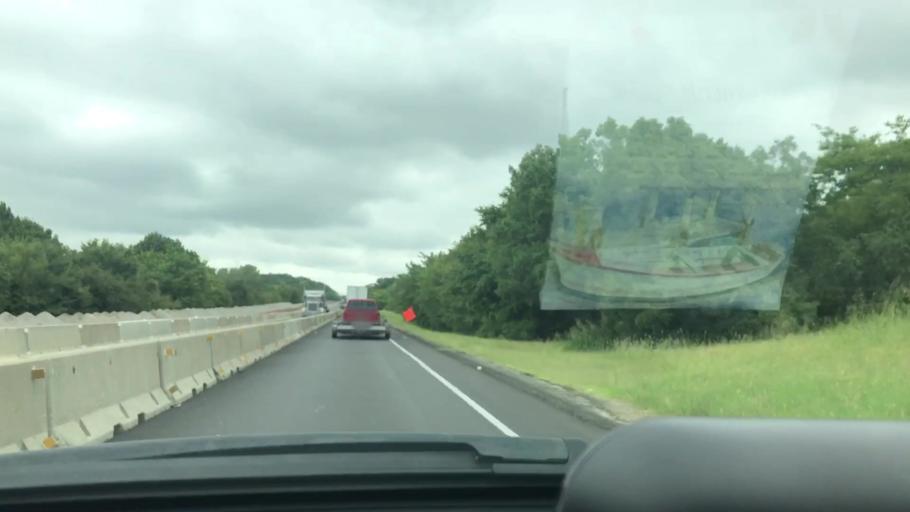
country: US
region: Oklahoma
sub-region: McIntosh County
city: Eufaula
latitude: 35.2630
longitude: -95.5893
